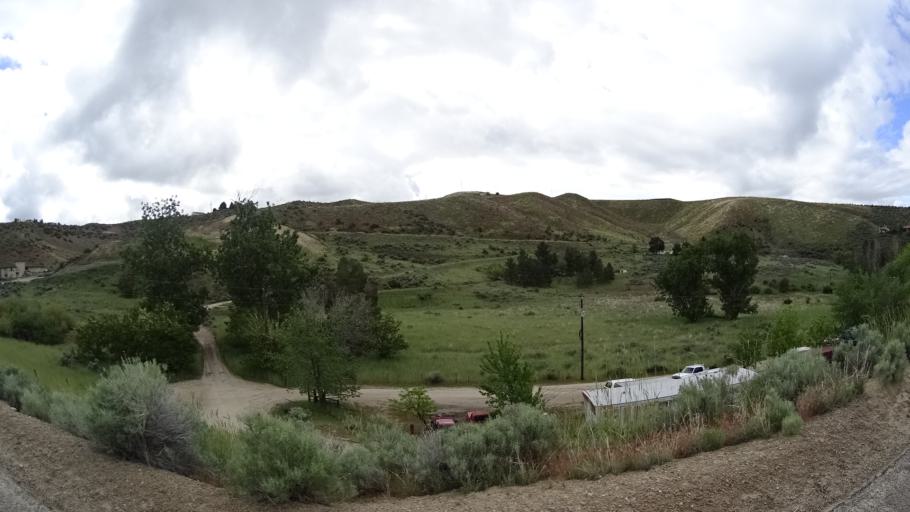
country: US
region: Idaho
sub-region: Ada County
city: Garden City
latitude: 43.6868
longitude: -116.2508
